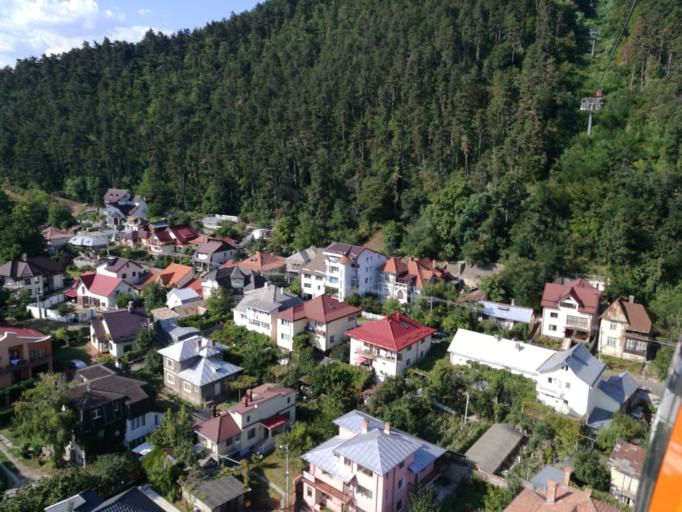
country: RO
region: Neamt
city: Piatra Neamt
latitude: 46.9364
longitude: 26.3644
